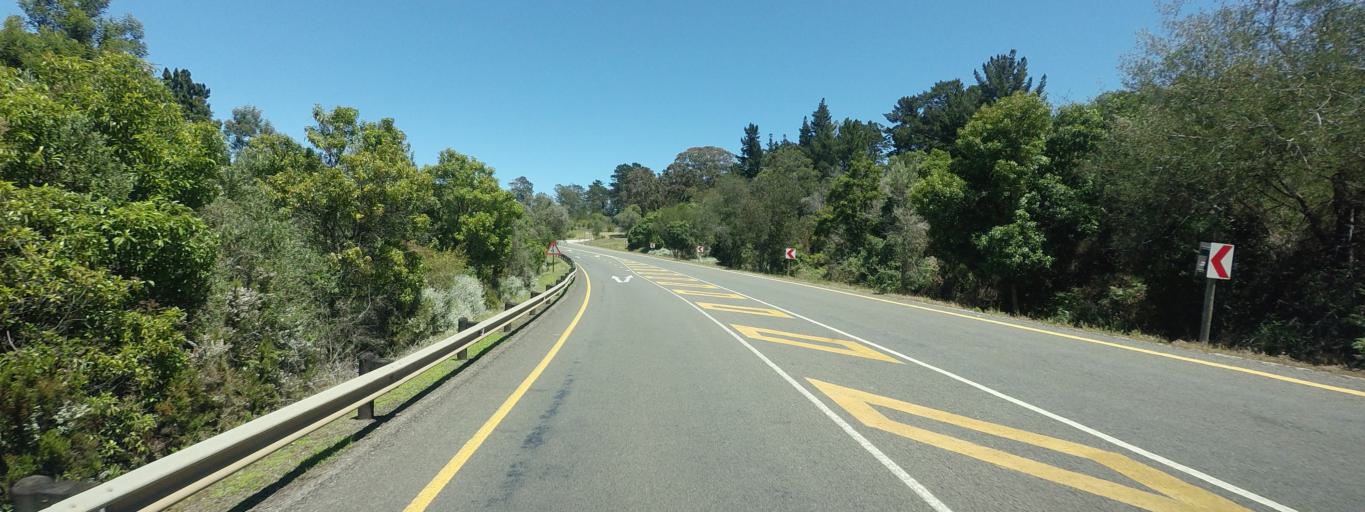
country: ZA
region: Western Cape
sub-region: Eden District Municipality
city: Plettenberg Bay
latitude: -33.9656
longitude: 23.4506
